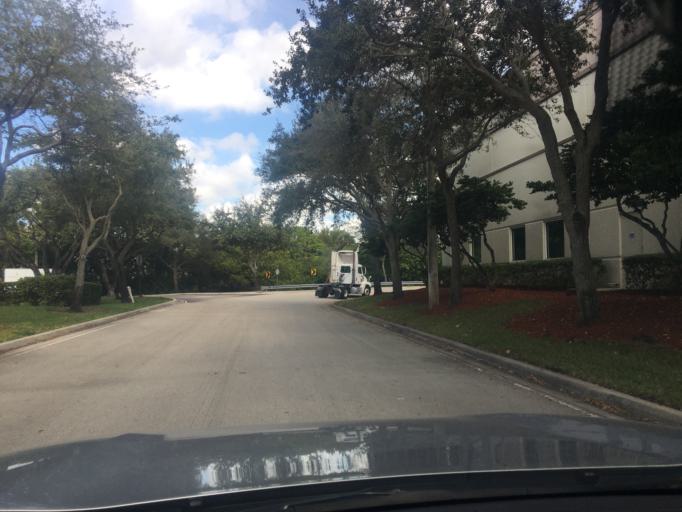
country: US
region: Florida
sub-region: Broward County
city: Broadview Park
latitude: 26.0709
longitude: -80.1804
